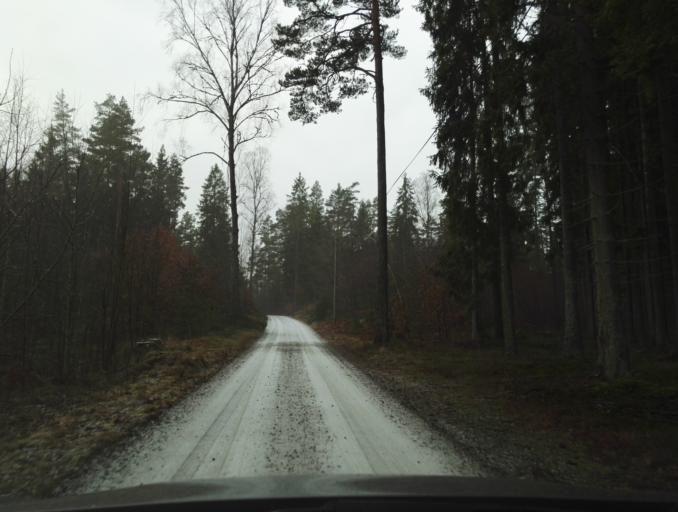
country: SE
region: Kronoberg
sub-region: Vaxjo Kommun
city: Vaexjoe
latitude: 56.9209
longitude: 14.7507
